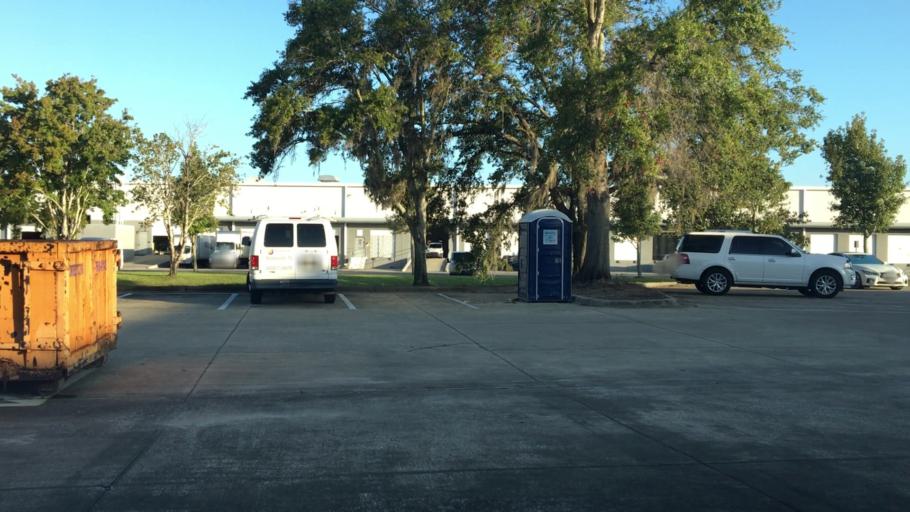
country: US
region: Florida
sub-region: Orange County
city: Conway
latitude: 28.4600
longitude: -81.2972
